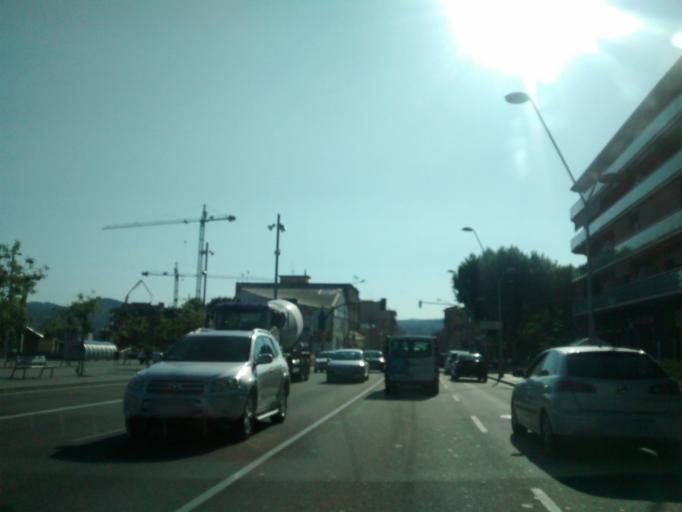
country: ES
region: Catalonia
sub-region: Provincia de Barcelona
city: Sant Feliu de Llobregat
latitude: 41.3796
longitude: 2.0534
